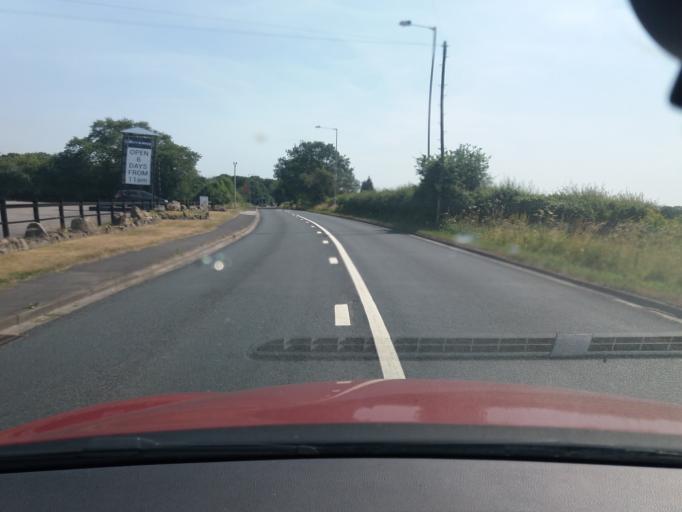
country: GB
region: England
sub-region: Lancashire
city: Coppull
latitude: 53.6415
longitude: -2.6791
